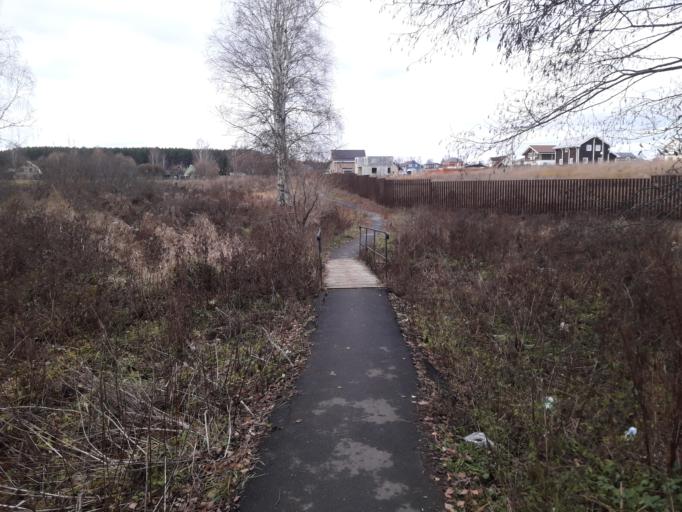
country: RU
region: Moskovskaya
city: Ashukino
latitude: 56.1669
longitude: 37.9344
